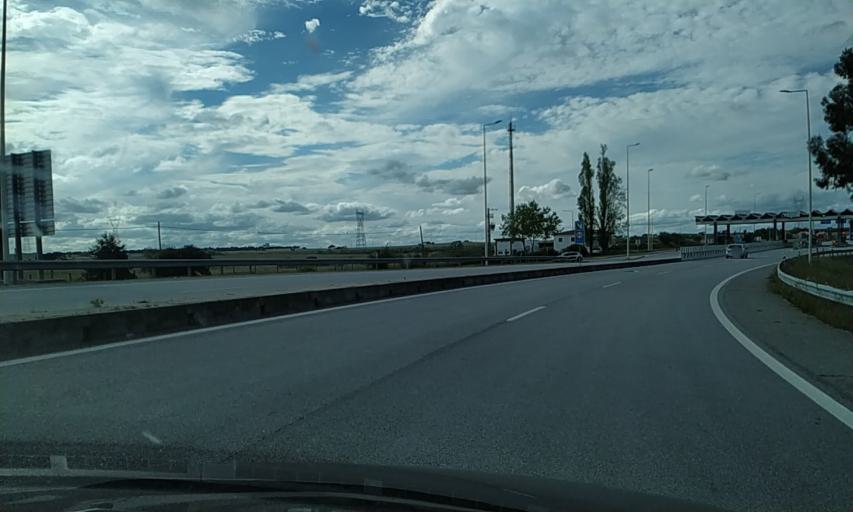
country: PT
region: Evora
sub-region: Evora
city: Evora
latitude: 38.6424
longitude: -7.8543
